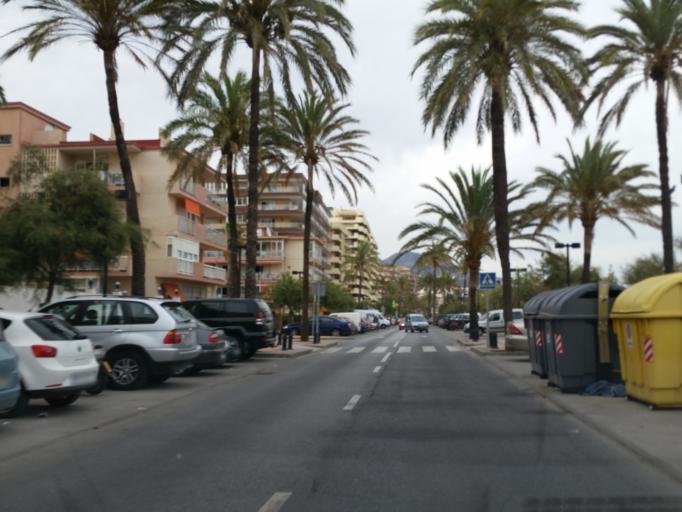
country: ES
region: Andalusia
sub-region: Provincia de Malaga
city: Fuengirola
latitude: 36.5568
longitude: -4.6105
